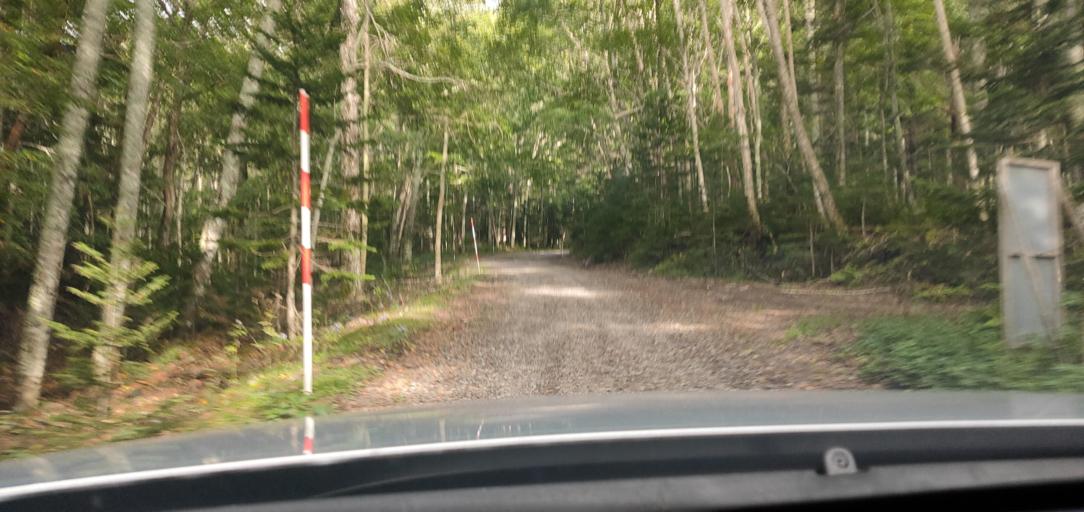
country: JP
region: Hokkaido
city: Kitami
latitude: 43.3748
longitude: 143.9632
